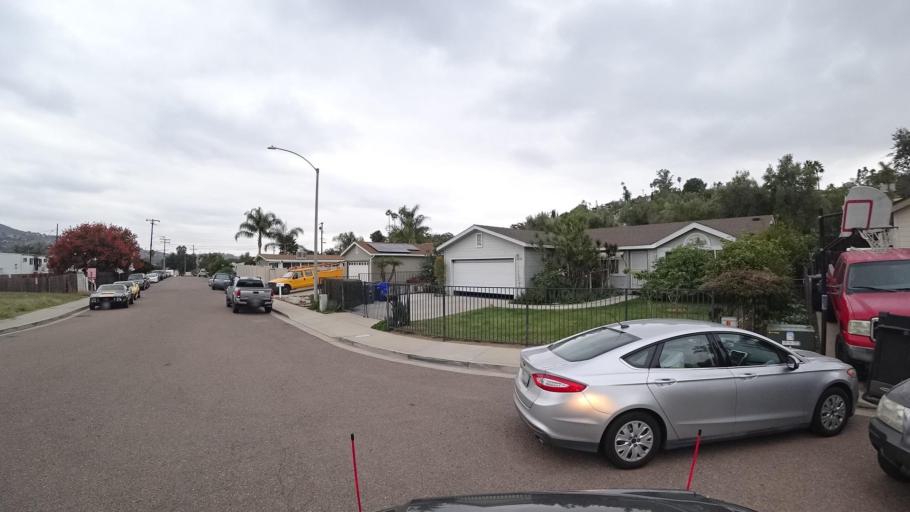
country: US
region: California
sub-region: San Diego County
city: Spring Valley
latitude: 32.7459
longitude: -117.0047
